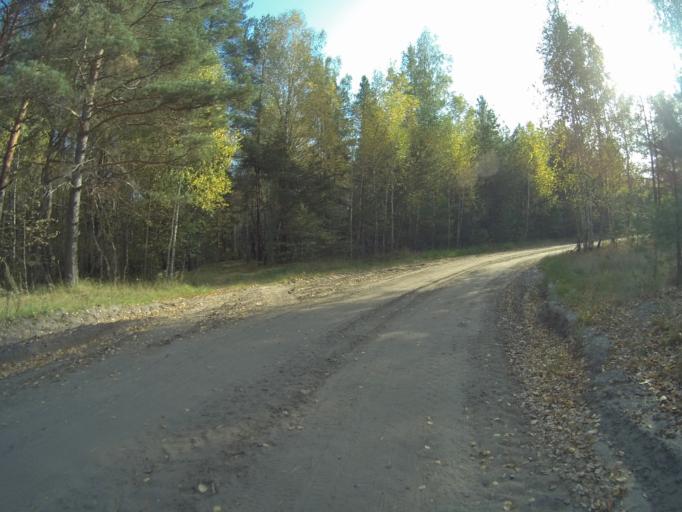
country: RU
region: Vladimir
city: Urshel'skiy
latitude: 55.8245
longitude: 40.1614
